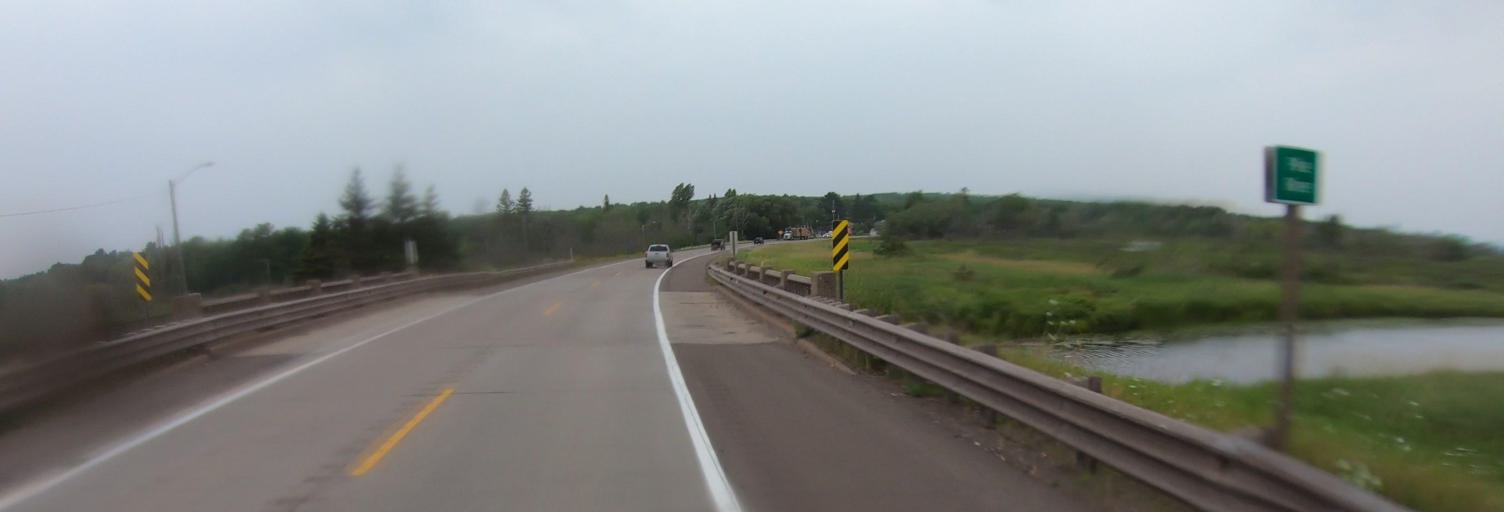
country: US
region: Michigan
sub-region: Houghton County
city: Dollar Bay
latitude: 47.0185
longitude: -88.5249
